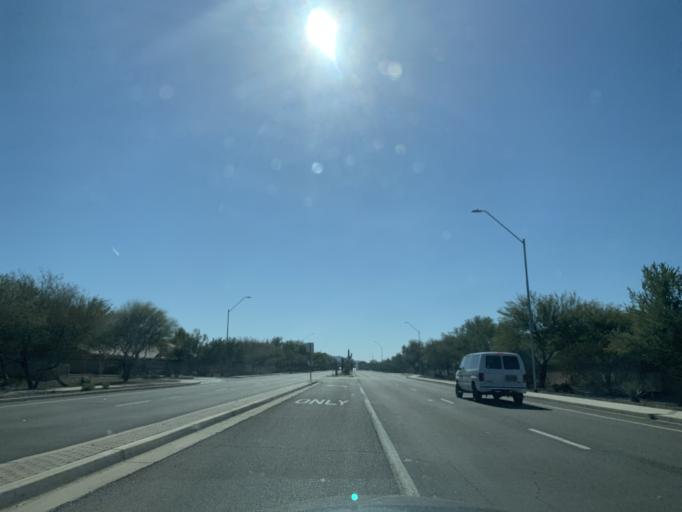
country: US
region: Arizona
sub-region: Pinal County
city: Casa Grande
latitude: 32.8924
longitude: -111.7227
